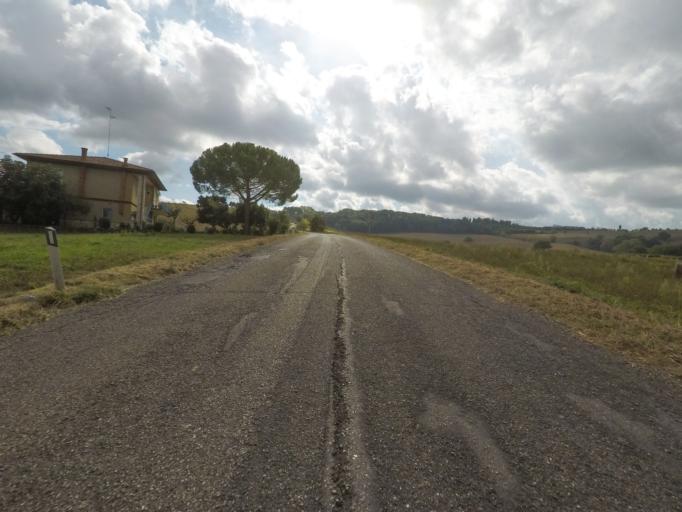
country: IT
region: Tuscany
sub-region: Provincia di Siena
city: Torrita di Siena
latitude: 43.1593
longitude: 11.7737
